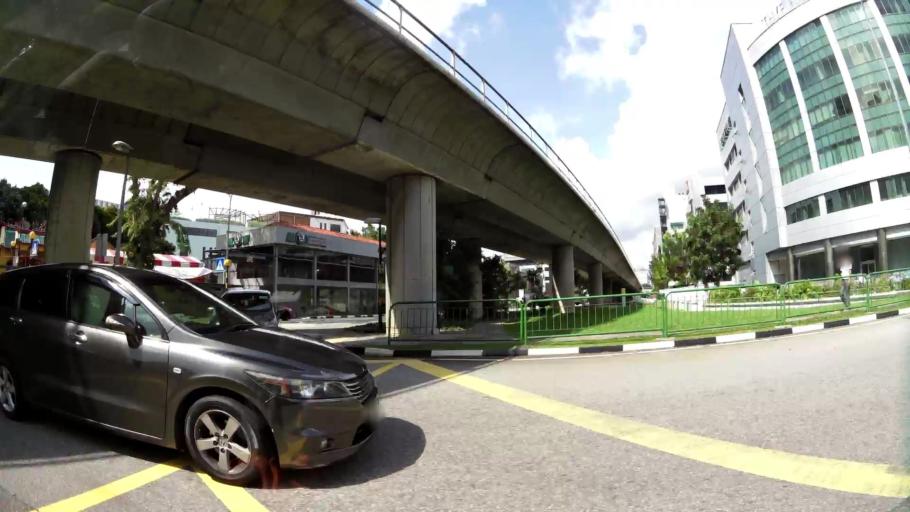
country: SG
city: Singapore
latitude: 1.2904
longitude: 103.8153
